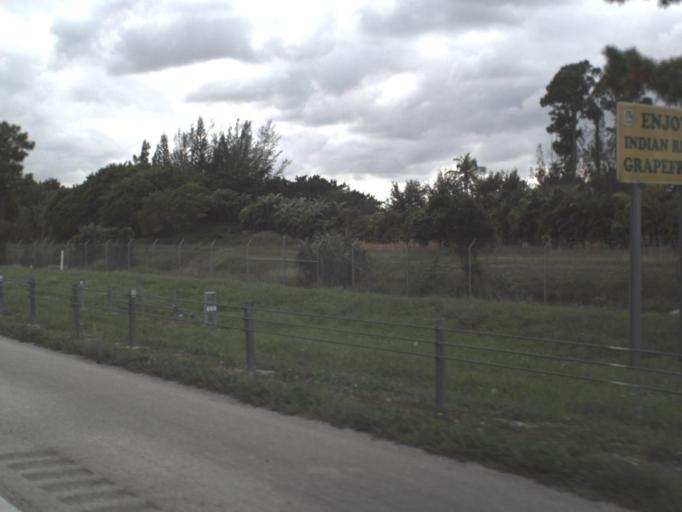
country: US
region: Florida
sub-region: Palm Beach County
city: Lake Belvedere Estates
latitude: 26.6592
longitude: -80.1743
